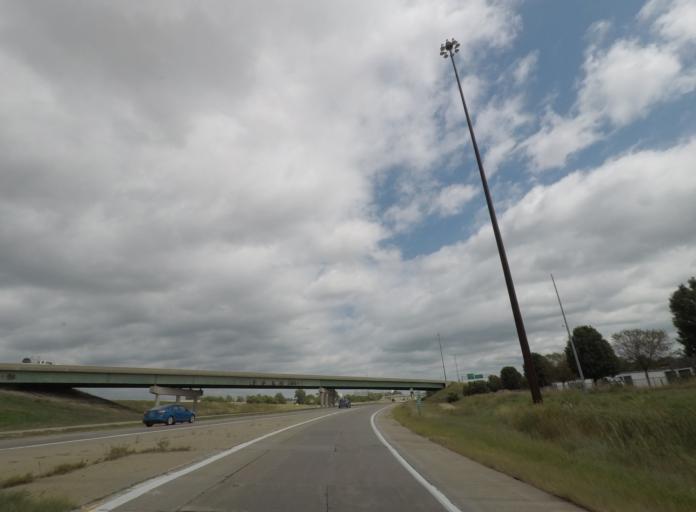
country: US
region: Iowa
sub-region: Linn County
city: Cedar Rapids
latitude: 41.9267
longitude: -91.6659
